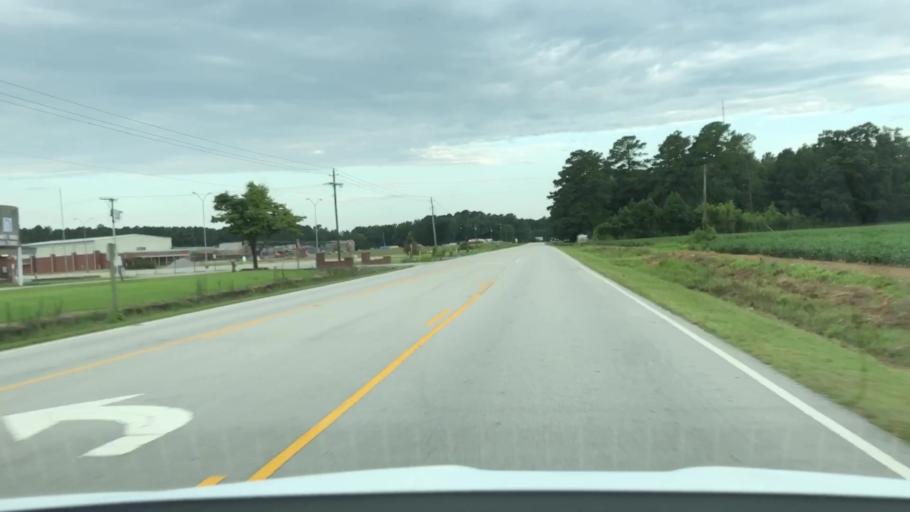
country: US
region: North Carolina
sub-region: Jones County
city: Trenton
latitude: 35.0349
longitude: -77.3330
